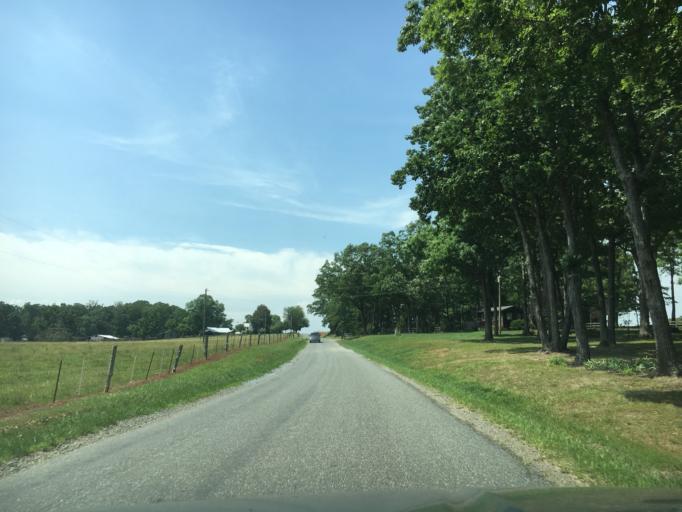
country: US
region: Virginia
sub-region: Pittsylvania County
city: Gretna
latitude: 36.9033
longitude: -79.4077
